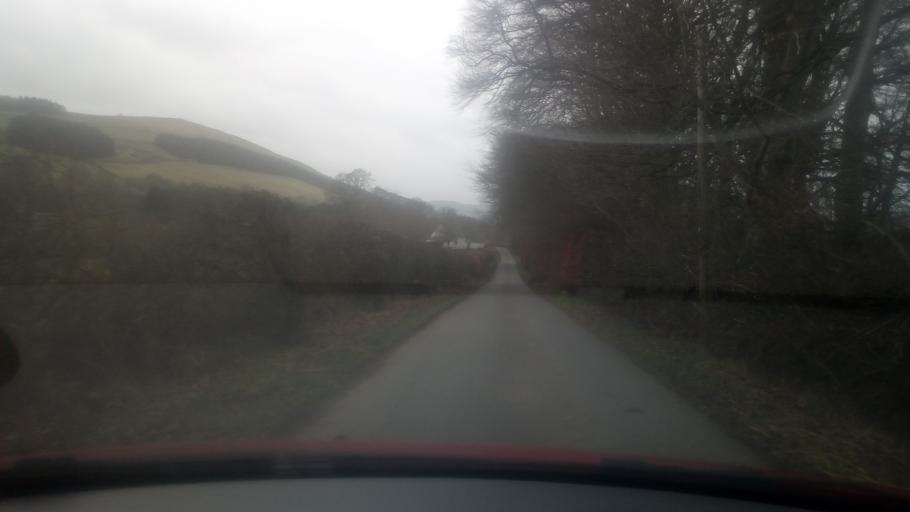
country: GB
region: Scotland
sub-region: The Scottish Borders
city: Jedburgh
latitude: 55.4134
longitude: -2.6475
